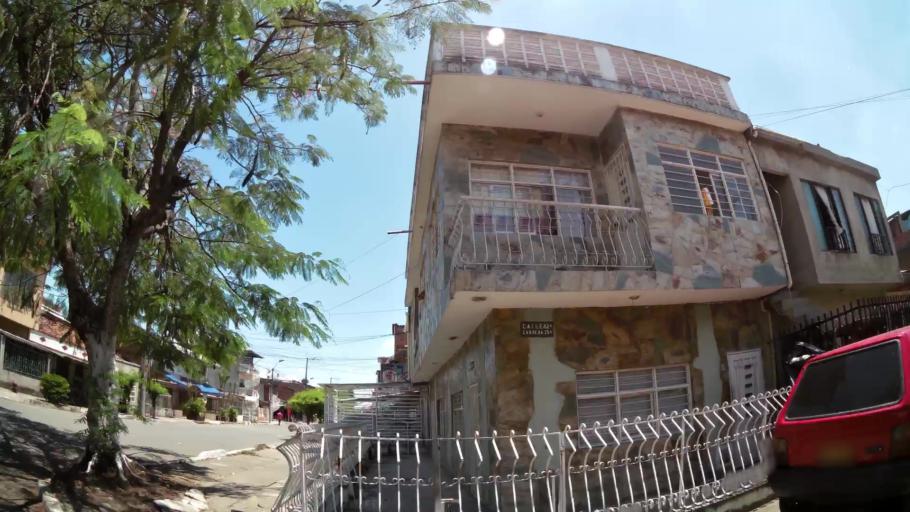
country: CO
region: Valle del Cauca
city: Cali
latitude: 3.4362
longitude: -76.5018
